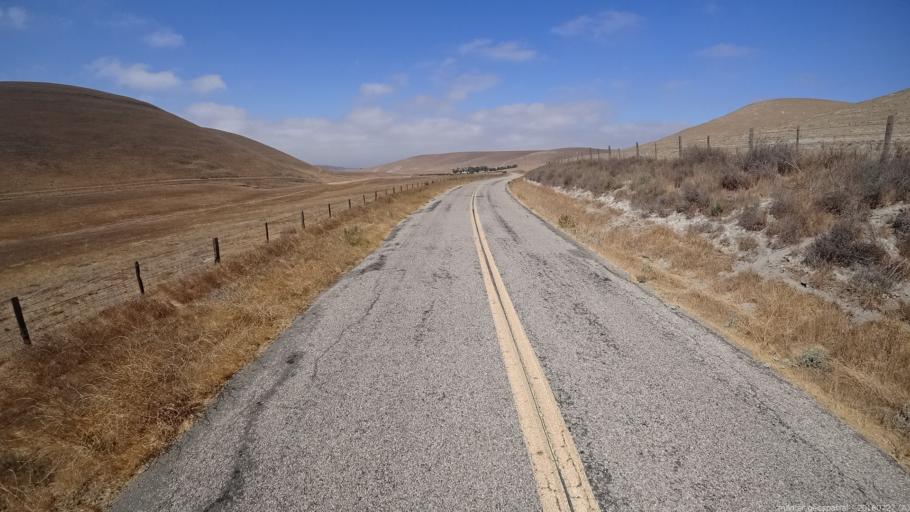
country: US
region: California
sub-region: Monterey County
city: King City
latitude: 36.2466
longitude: -121.0282
